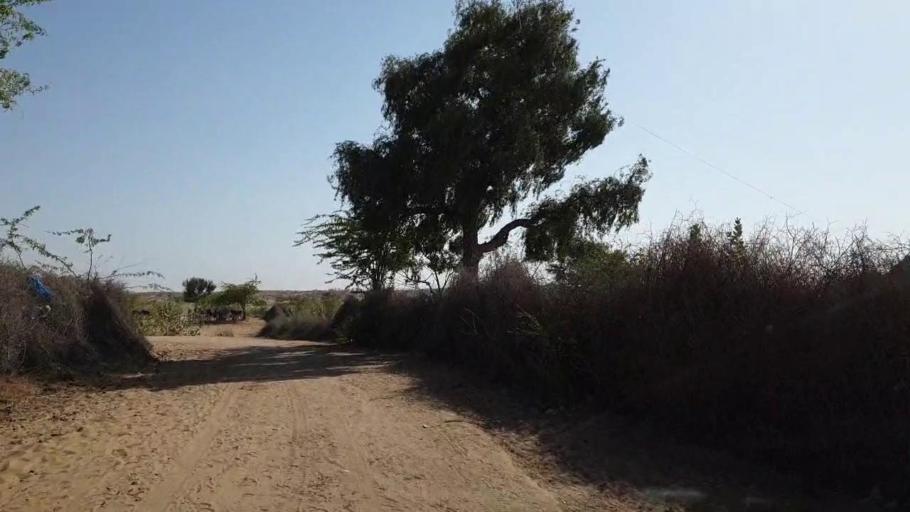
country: PK
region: Sindh
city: Umarkot
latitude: 25.1438
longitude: 70.0650
